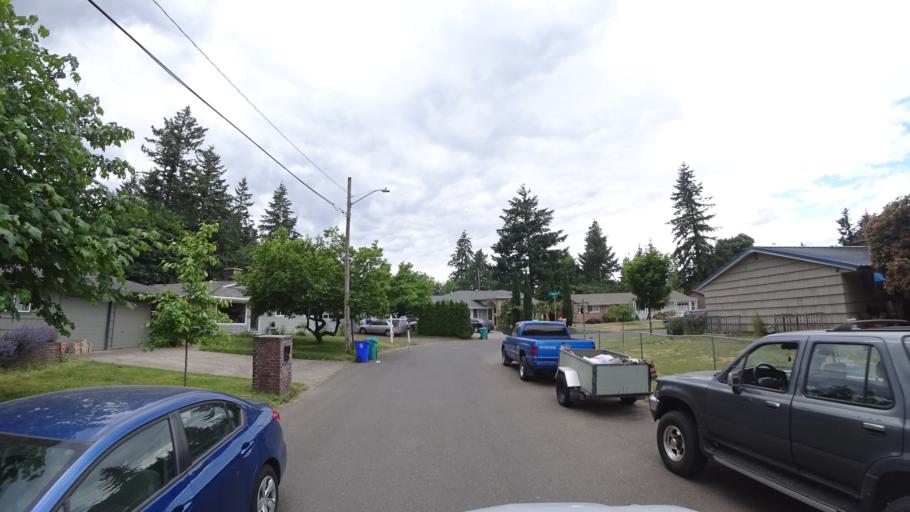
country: US
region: Oregon
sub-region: Clackamas County
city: Happy Valley
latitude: 45.5015
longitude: -122.5042
